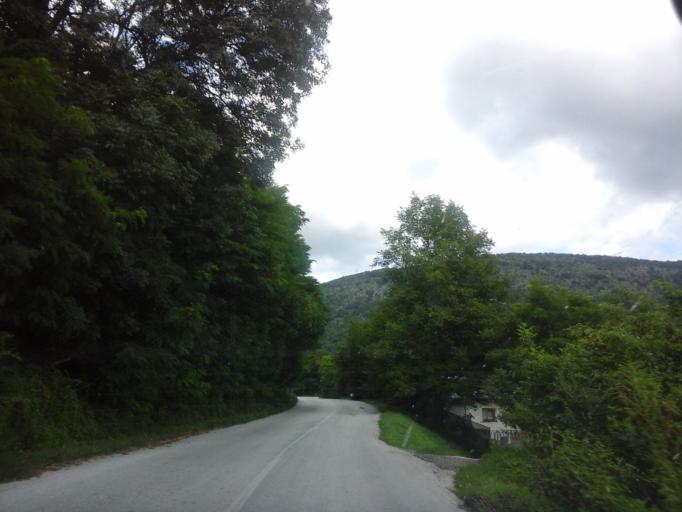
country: SK
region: Kosicky
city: Roznava
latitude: 48.5517
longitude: 20.4000
